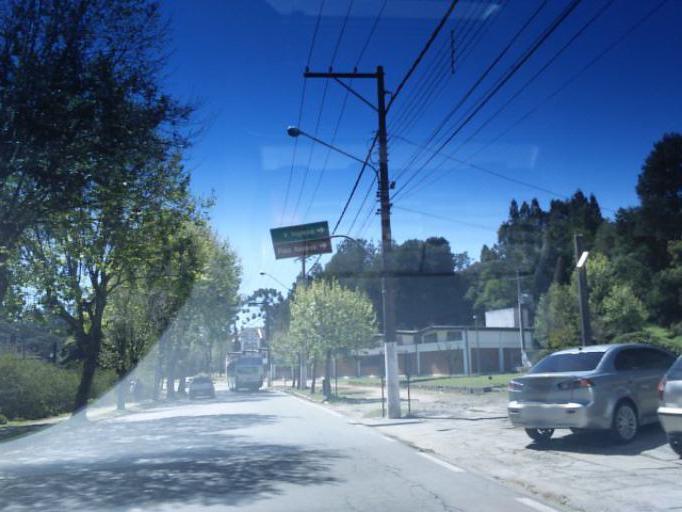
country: BR
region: Sao Paulo
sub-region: Campos Do Jordao
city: Campos do Jordao
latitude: -22.7284
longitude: -45.5817
